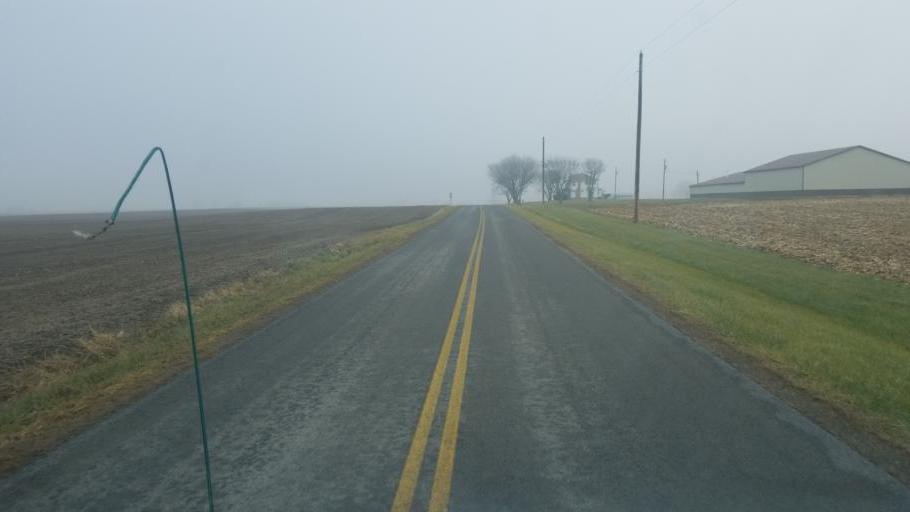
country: US
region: Ohio
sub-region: Hardin County
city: Kenton
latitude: 40.4906
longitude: -83.5457
